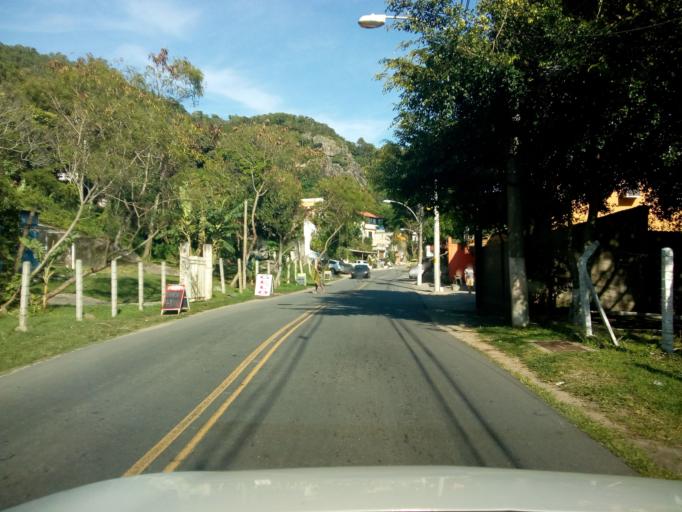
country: BR
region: Rio de Janeiro
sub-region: Nilopolis
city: Nilopolis
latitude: -23.0302
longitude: -43.4972
